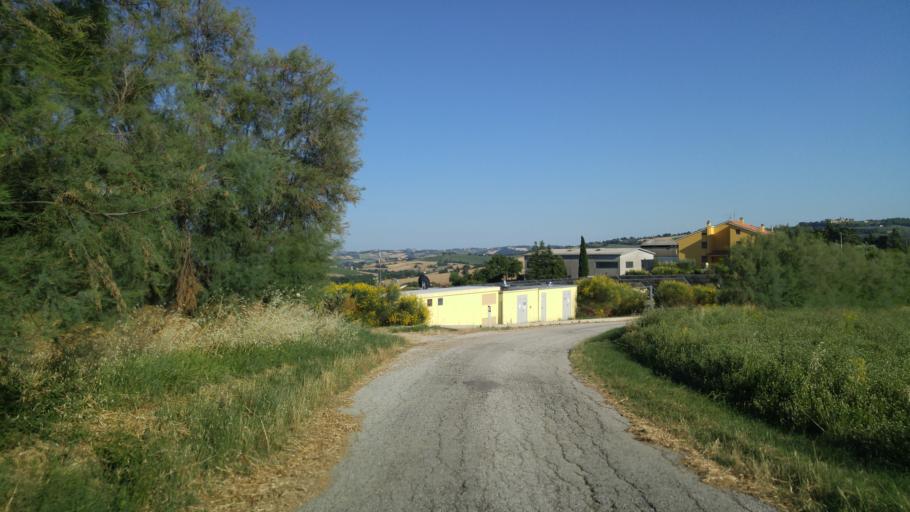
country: IT
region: The Marches
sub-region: Provincia di Pesaro e Urbino
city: Cartoceto
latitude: 43.7923
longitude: 12.8864
